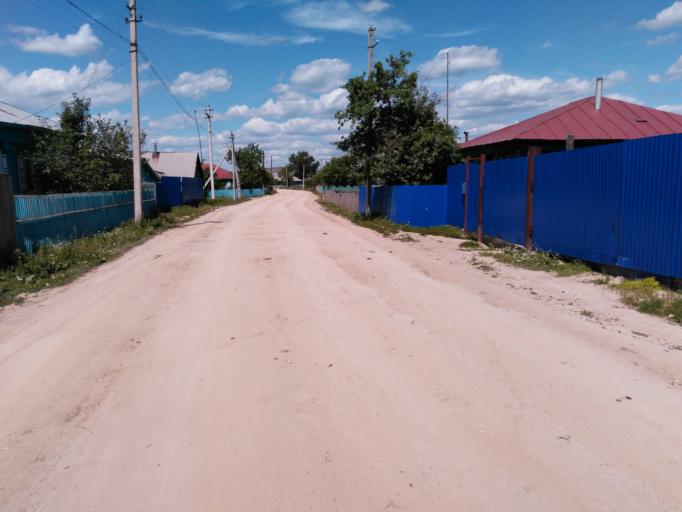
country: RU
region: Bashkortostan
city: Akhunovo
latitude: 54.2075
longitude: 59.6081
